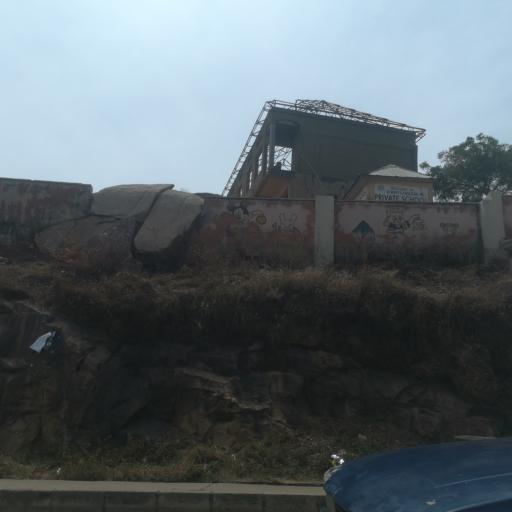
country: NG
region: Plateau
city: Jos
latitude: 9.9289
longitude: 8.8667
